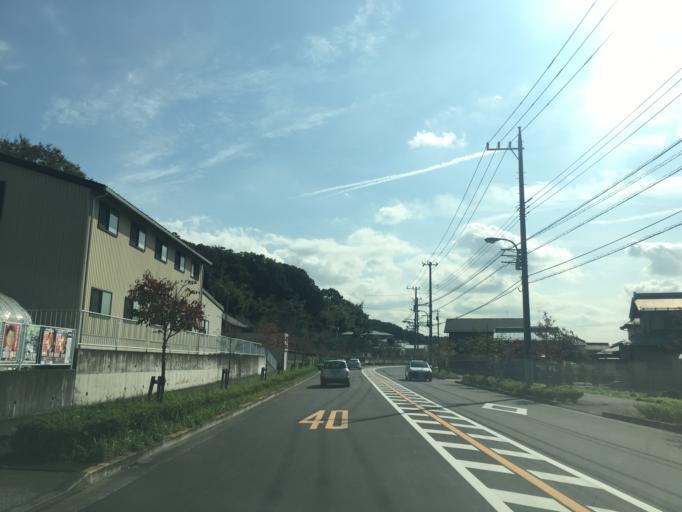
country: JP
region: Tokyo
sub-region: Machida-shi
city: Machida
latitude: 35.5936
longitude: 139.4143
